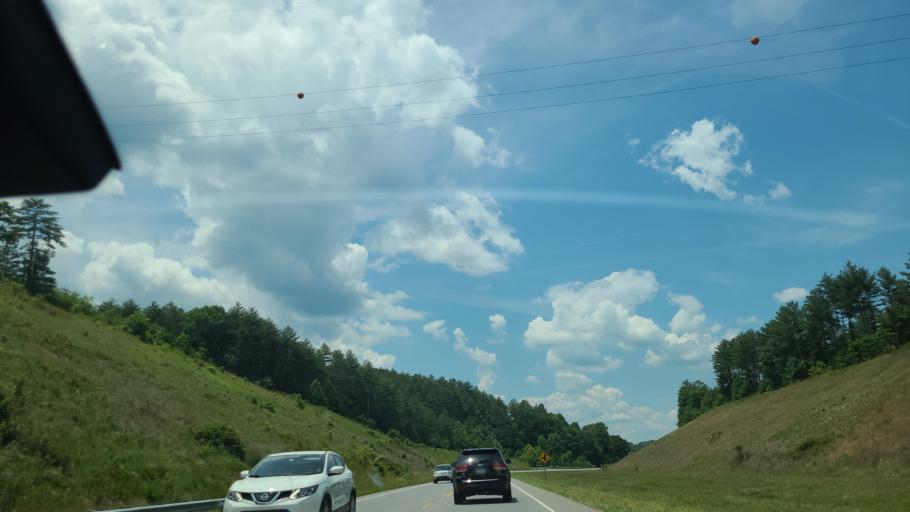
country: US
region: North Carolina
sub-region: Cherokee County
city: Murphy
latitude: 35.0733
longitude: -84.0215
